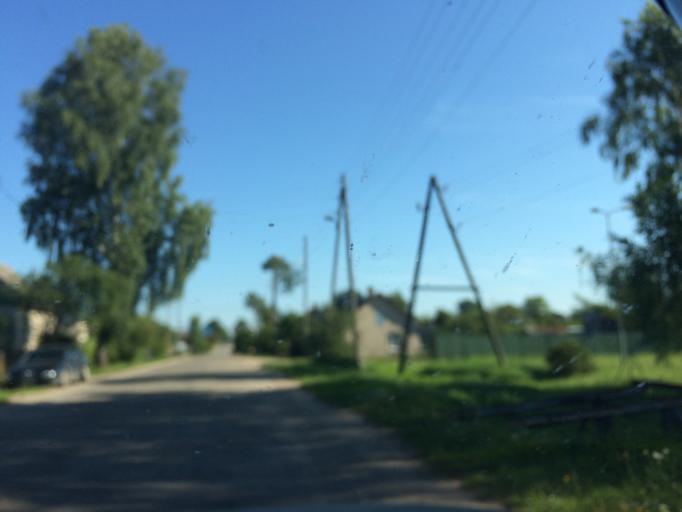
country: LV
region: Rezekne
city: Rezekne
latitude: 56.4884
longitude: 27.3349
